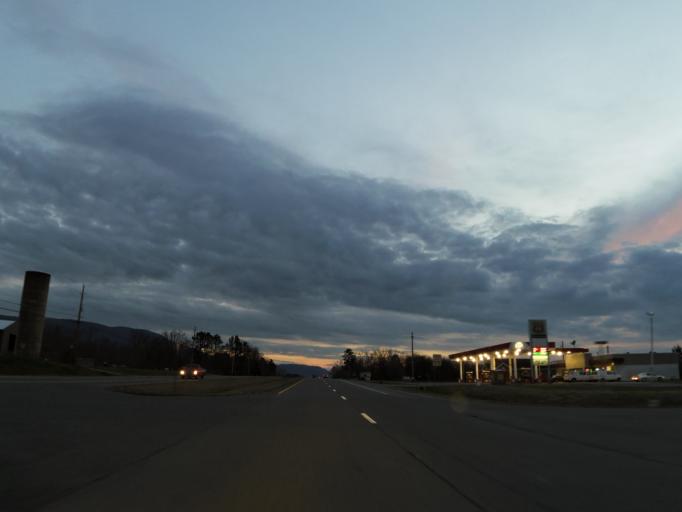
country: US
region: Tennessee
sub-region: McMinn County
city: Etowah
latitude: 35.2625
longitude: -84.5503
